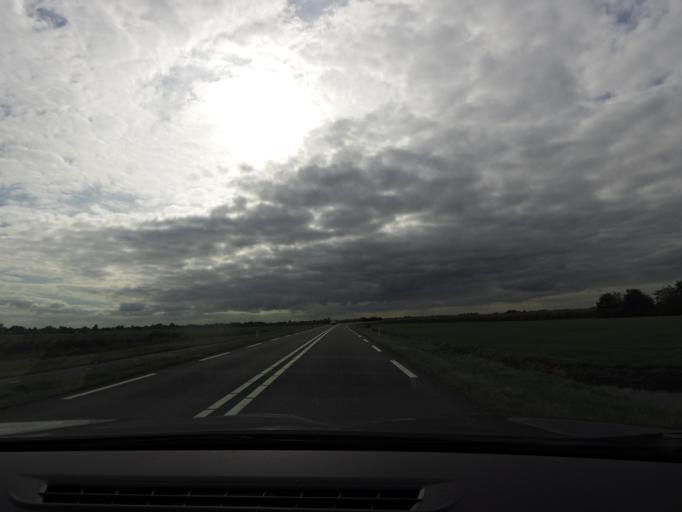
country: NL
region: Utrecht
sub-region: Gemeente Lopik
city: Lopik
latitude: 51.9612
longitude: 4.9155
